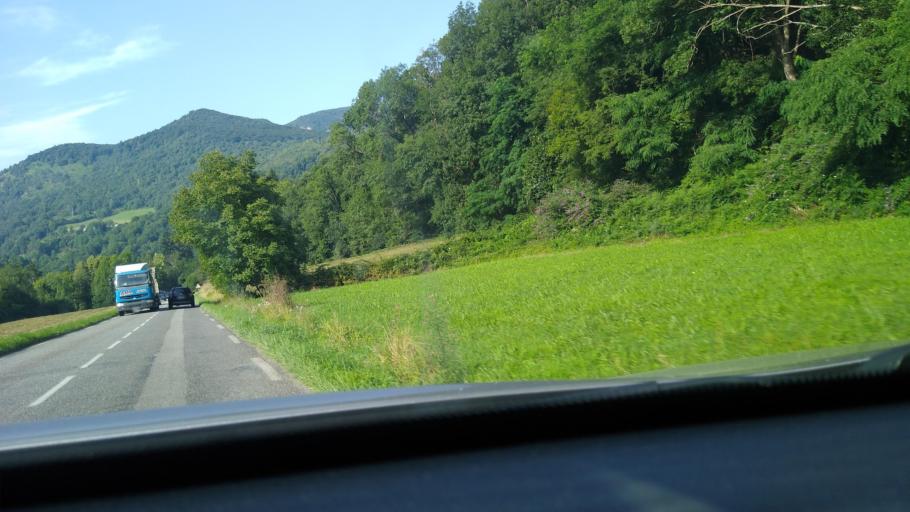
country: FR
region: Midi-Pyrenees
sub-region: Departement de l'Ariege
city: Saint-Girons
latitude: 42.9530
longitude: 1.1757
